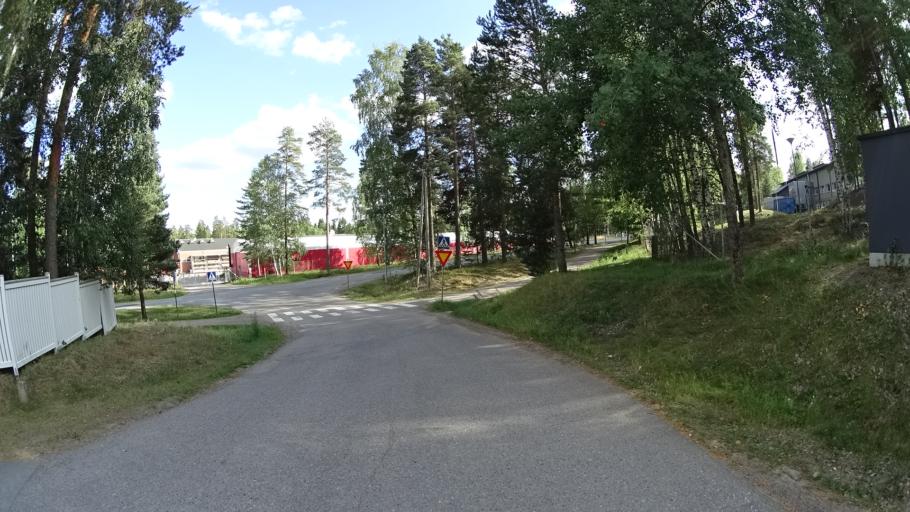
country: FI
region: Uusimaa
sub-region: Helsinki
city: Vihti
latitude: 60.3466
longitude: 24.3284
